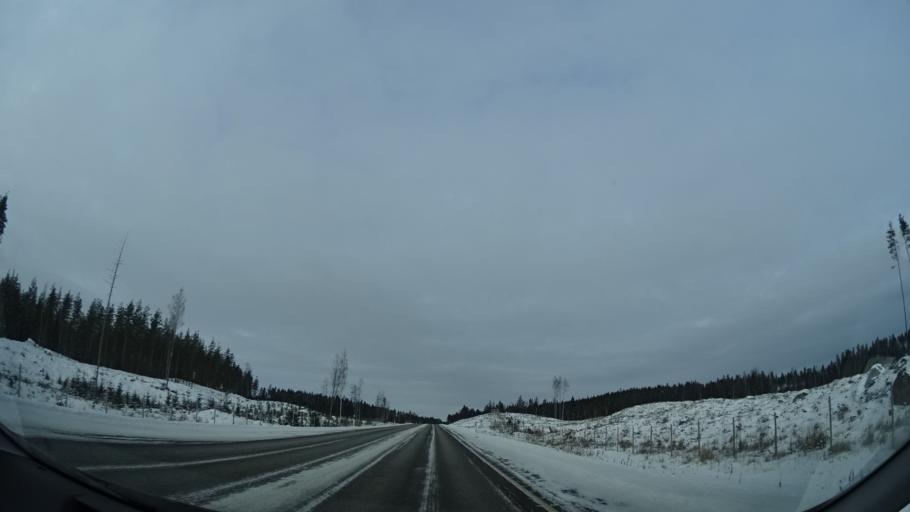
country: FI
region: Uusimaa
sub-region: Helsinki
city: Kaerkoelae
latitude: 60.6087
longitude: 24.0542
